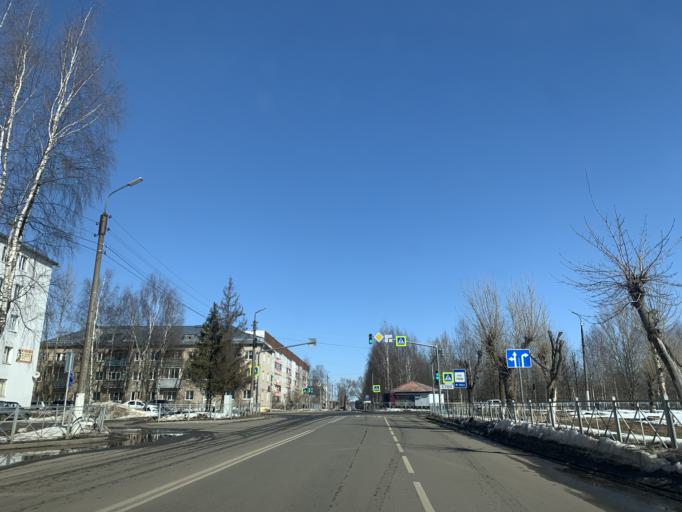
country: RU
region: Jaroslavl
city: Tutayev
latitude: 57.8696
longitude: 39.5136
